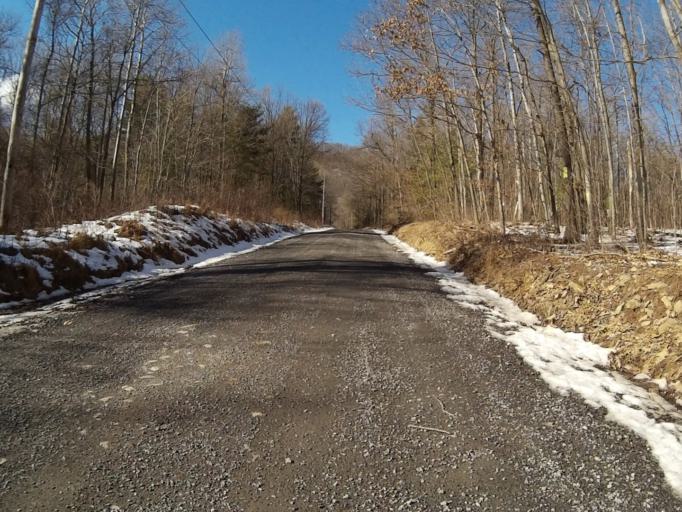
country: US
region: Pennsylvania
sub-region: Centre County
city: Stormstown
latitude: 40.8544
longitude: -78.0521
